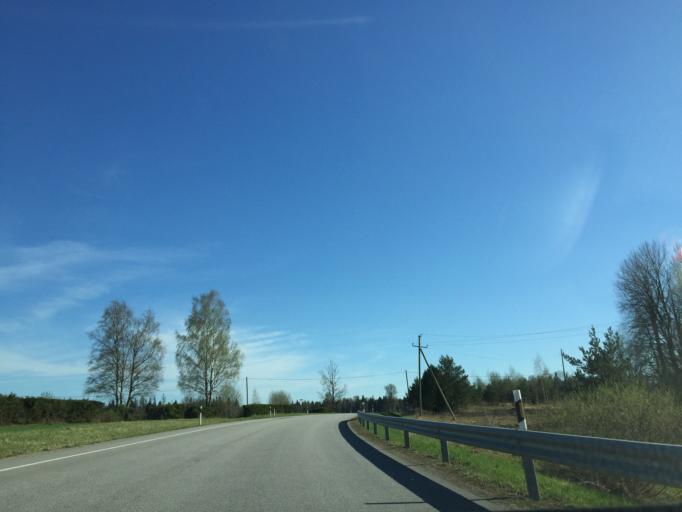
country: EE
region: Vorumaa
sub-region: Antsla vald
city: Vana-Antsla
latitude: 57.8977
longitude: 26.2895
